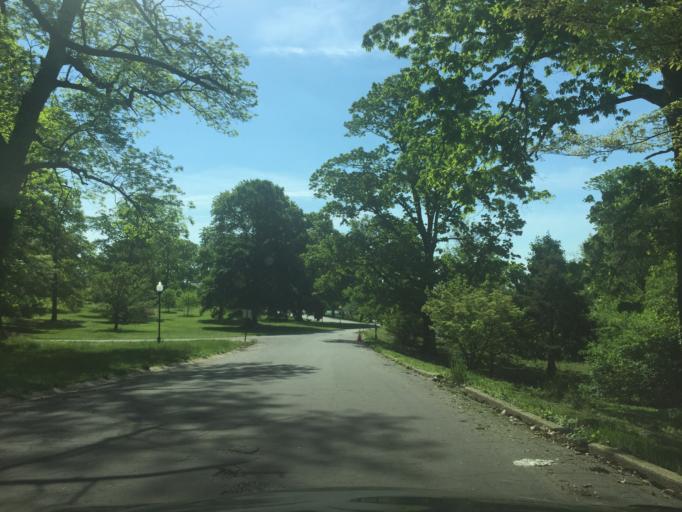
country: US
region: Maryland
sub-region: City of Baltimore
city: Baltimore
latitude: 39.3206
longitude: -76.6435
